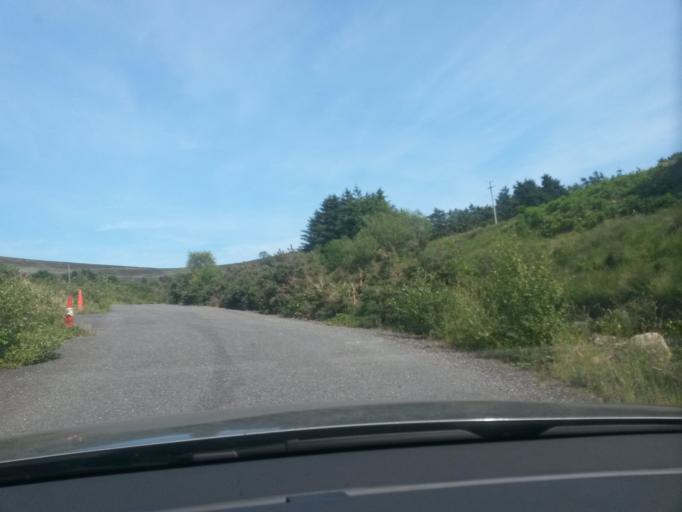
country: IE
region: Leinster
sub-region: Wicklow
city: Blessington
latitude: 53.1347
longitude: -6.4743
